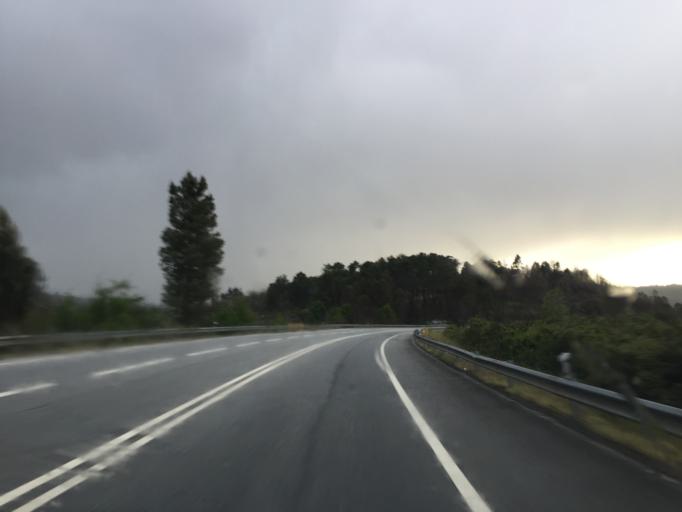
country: PT
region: Viseu
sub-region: Viseu
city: Viseu
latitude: 40.6079
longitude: -7.9633
